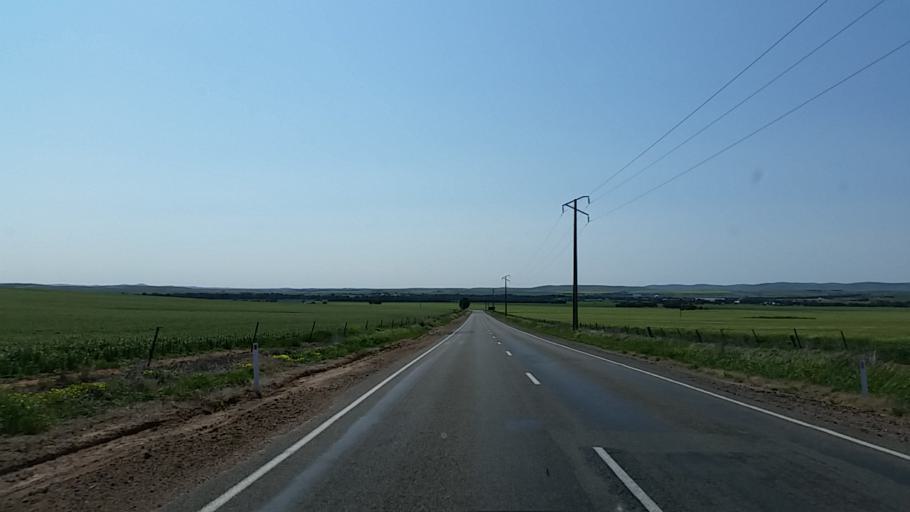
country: AU
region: South Australia
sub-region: Port Pirie City and Dists
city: Crystal Brook
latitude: -33.2760
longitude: 138.3047
